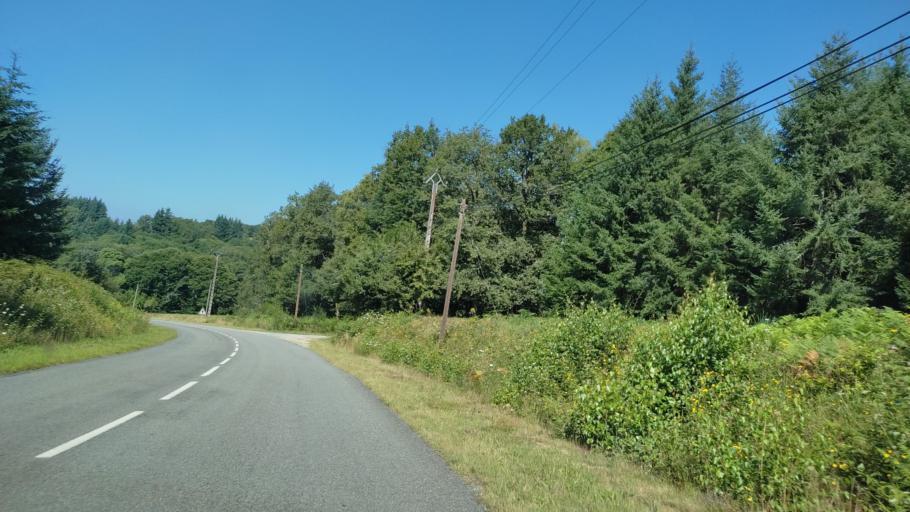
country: FR
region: Limousin
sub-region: Departement de la Haute-Vienne
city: Razes
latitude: 46.0372
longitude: 1.3199
